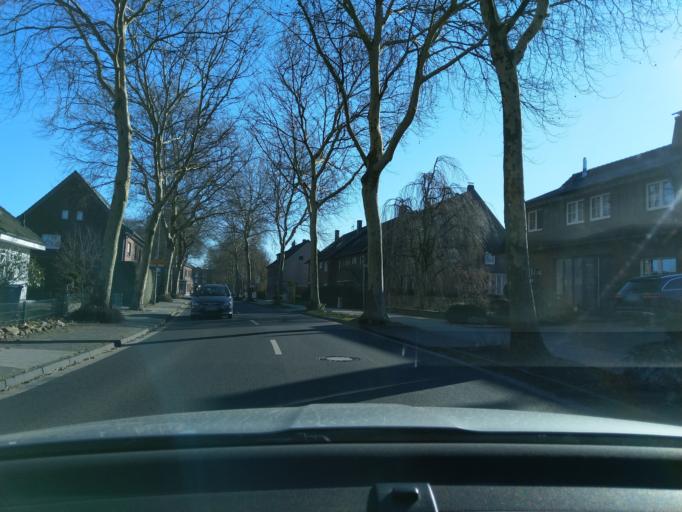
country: DE
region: North Rhine-Westphalia
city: Wegberg
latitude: 51.1373
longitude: 6.2919
